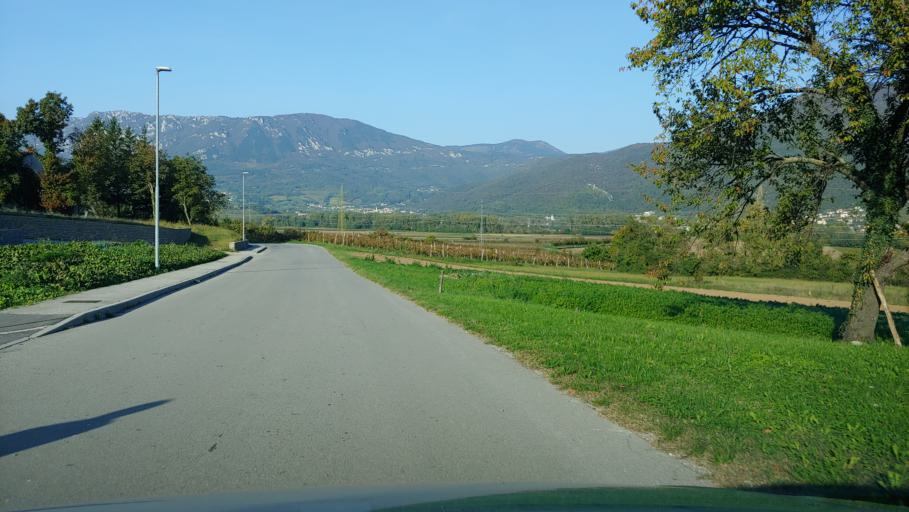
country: SI
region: Vipava
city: Vipava
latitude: 45.8289
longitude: 13.9390
